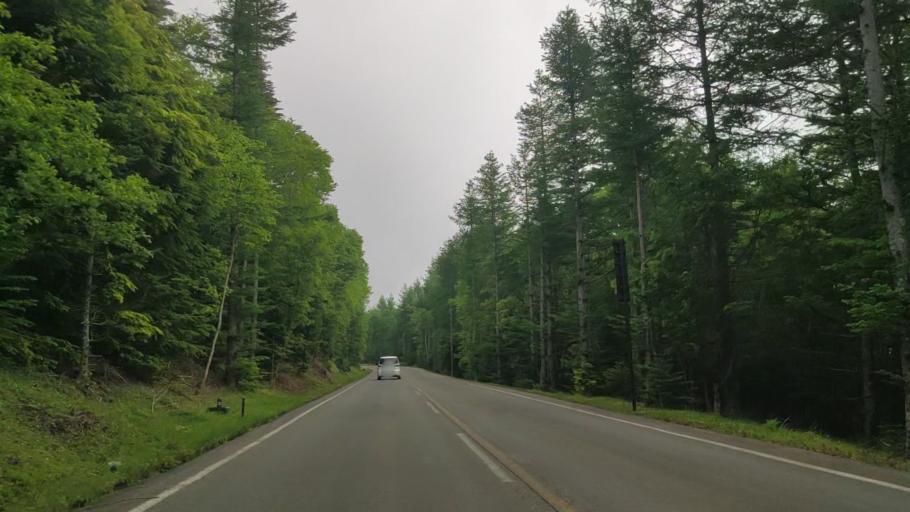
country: JP
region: Yamanashi
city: Fujikawaguchiko
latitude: 35.3799
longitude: 138.6906
